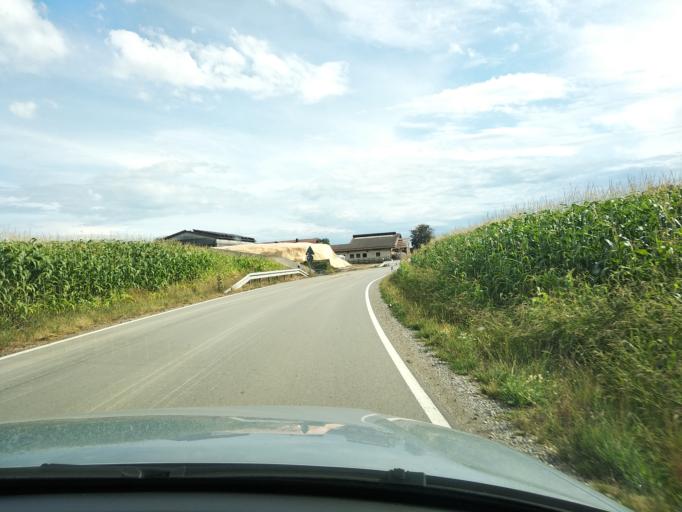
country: DE
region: Bavaria
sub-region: Swabia
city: Wolfertschwenden
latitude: 47.8714
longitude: 10.2371
